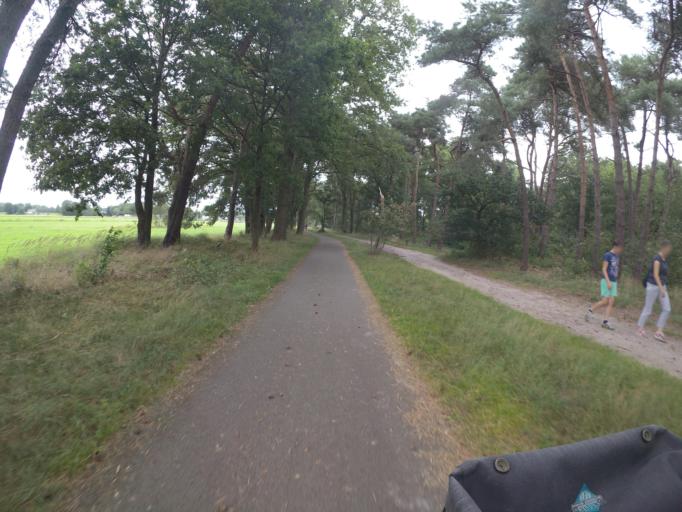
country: NL
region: North Brabant
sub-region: Gemeente Valkenswaard
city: Valkenswaard
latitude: 51.3328
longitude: 5.4437
